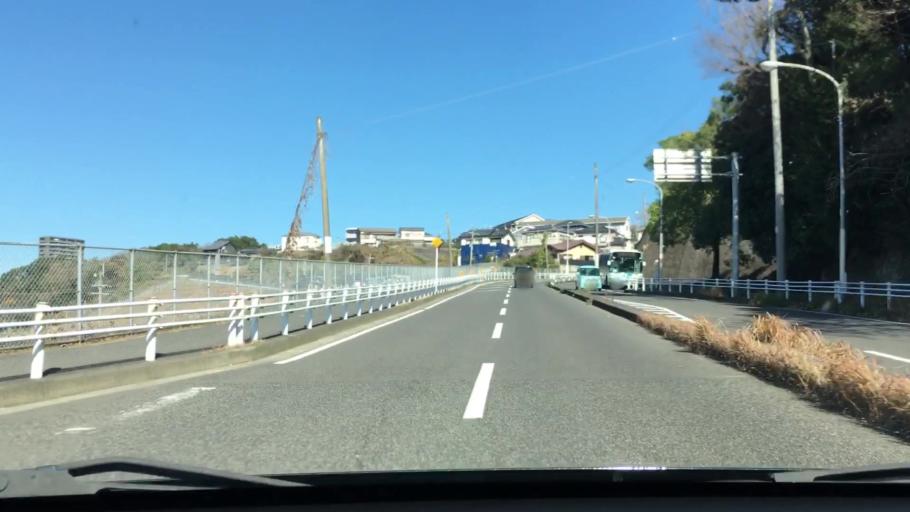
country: JP
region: Kagoshima
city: Kagoshima-shi
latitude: 31.5581
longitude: 130.5262
